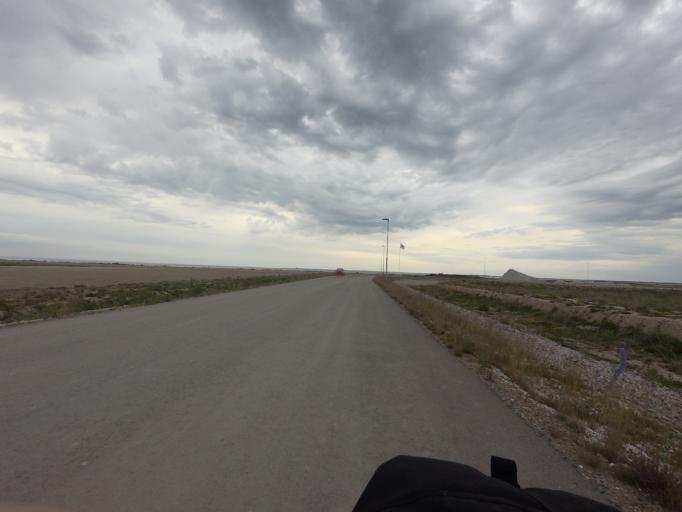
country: SE
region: Skane
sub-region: Malmo
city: Malmoe
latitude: 55.6330
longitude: 12.9947
